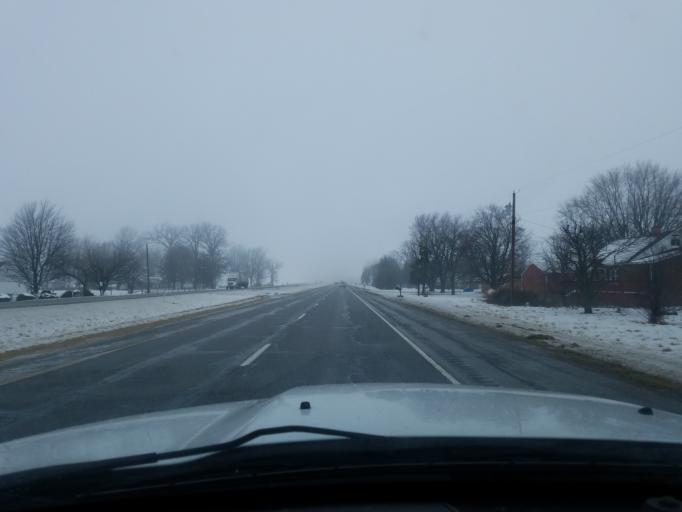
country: US
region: Indiana
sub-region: Tipton County
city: Tipton
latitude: 40.3088
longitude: -86.1268
